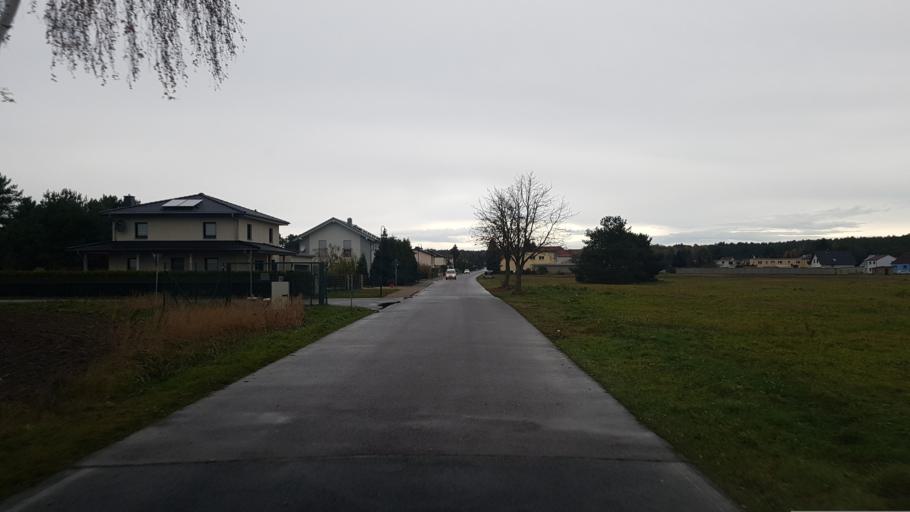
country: DE
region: Saxony-Anhalt
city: Abtsdorf
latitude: 51.8756
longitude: 12.7415
